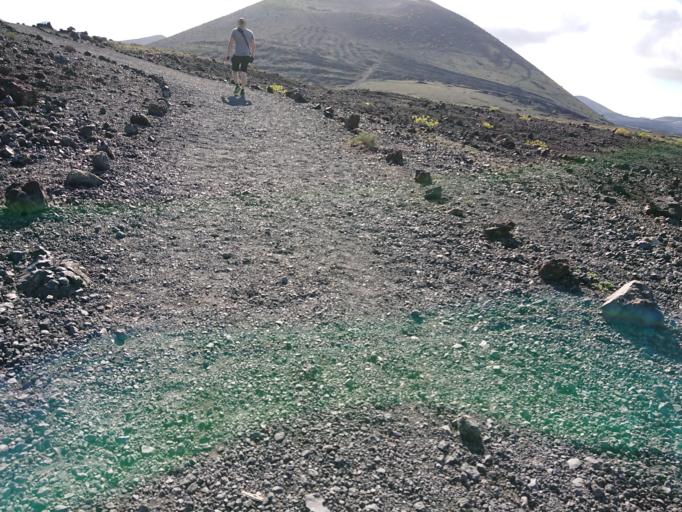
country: ES
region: Canary Islands
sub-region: Provincia de Las Palmas
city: Tias
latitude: 29.0034
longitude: -13.6817
